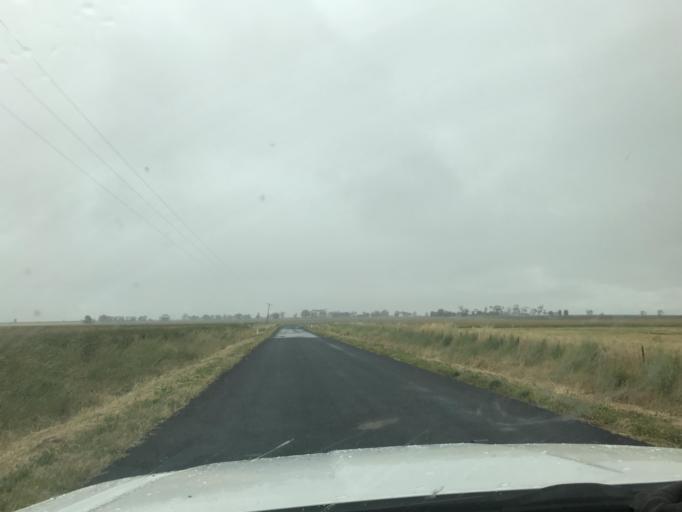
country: AU
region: South Australia
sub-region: Tatiara
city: Bordertown
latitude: -36.3466
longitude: 141.1353
